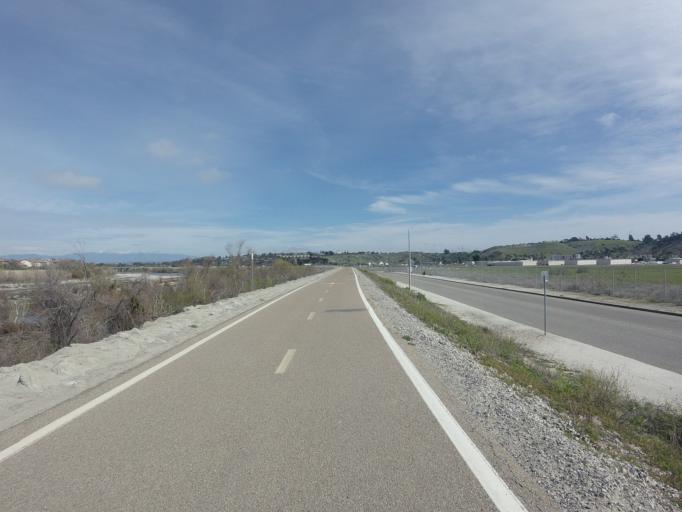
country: US
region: California
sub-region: San Diego County
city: Camp Pendleton South
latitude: 33.2206
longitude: -117.3526
